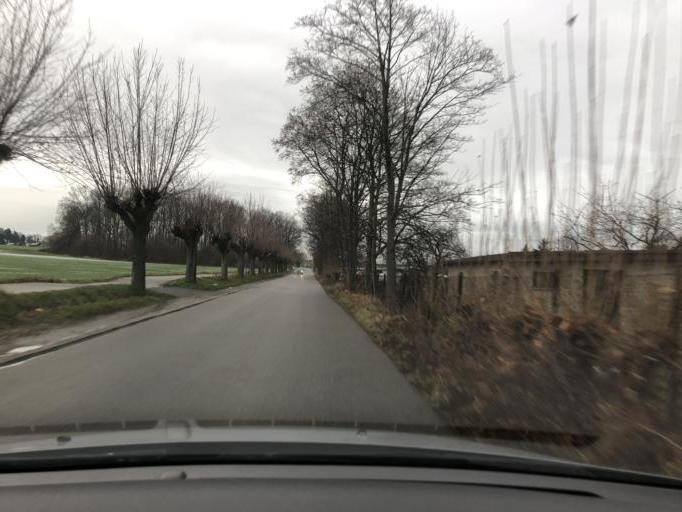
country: DE
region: Saxony
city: Limbach-Oberfrohna
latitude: 50.8578
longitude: 12.7296
